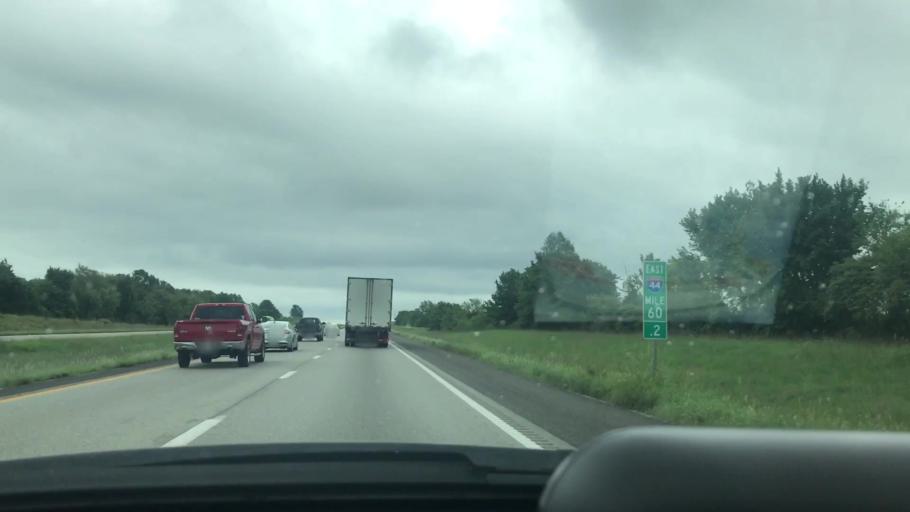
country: US
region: Missouri
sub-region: Christian County
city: Billings
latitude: 37.1863
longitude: -93.6015
